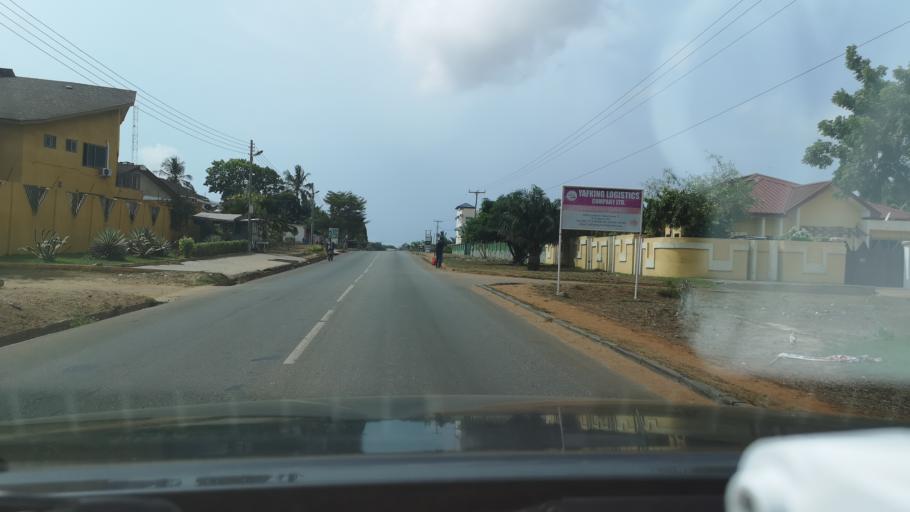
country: GH
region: Greater Accra
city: Tema
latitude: 5.6736
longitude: -0.0293
